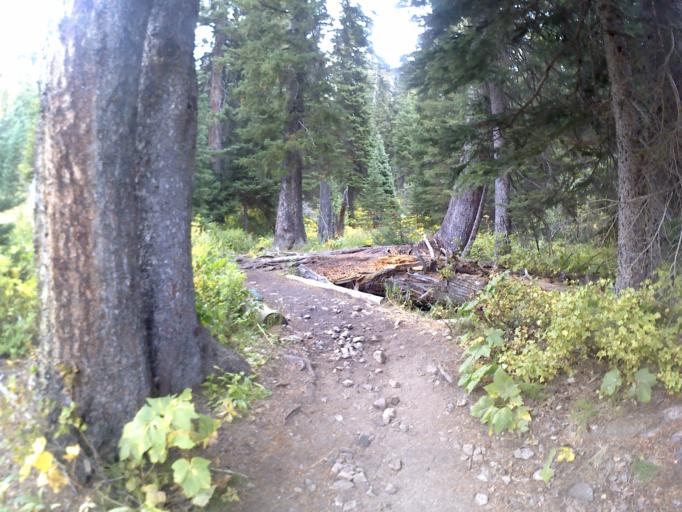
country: US
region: Wyoming
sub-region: Teton County
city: Moose Wilson Road
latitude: 43.7698
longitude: -110.7432
